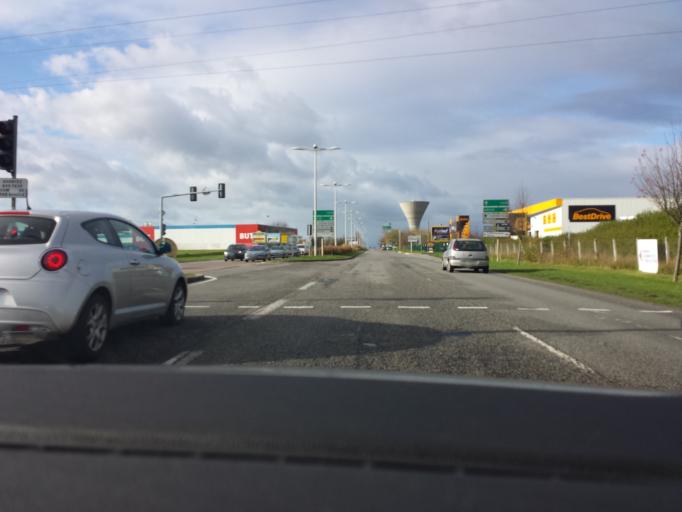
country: FR
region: Haute-Normandie
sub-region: Departement de l'Eure
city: Evreux
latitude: 49.0156
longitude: 1.1794
